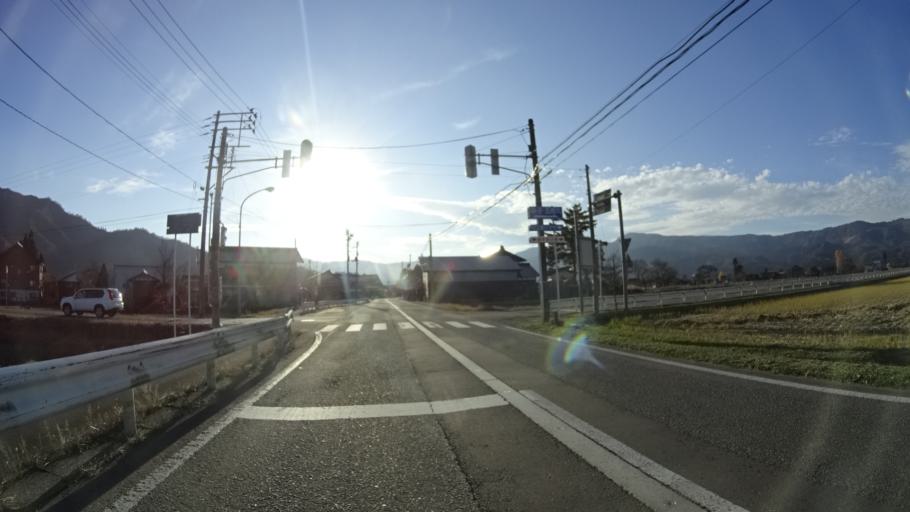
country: JP
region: Niigata
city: Shiozawa
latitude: 37.0092
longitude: 138.8478
